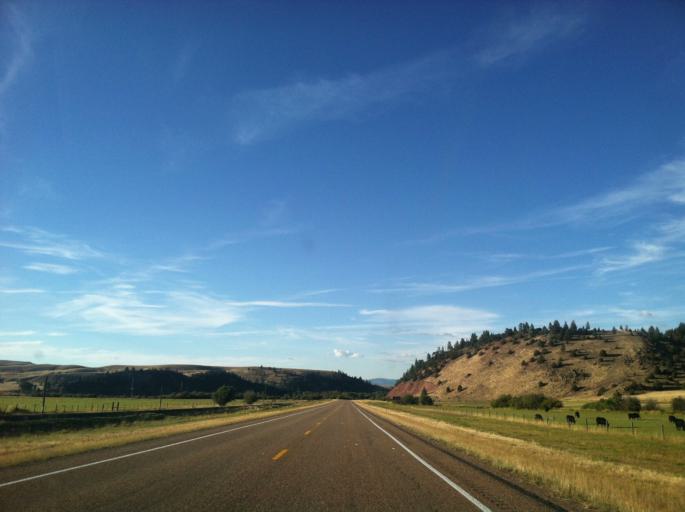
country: US
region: Montana
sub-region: Granite County
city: Philipsburg
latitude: 46.5070
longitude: -113.2254
